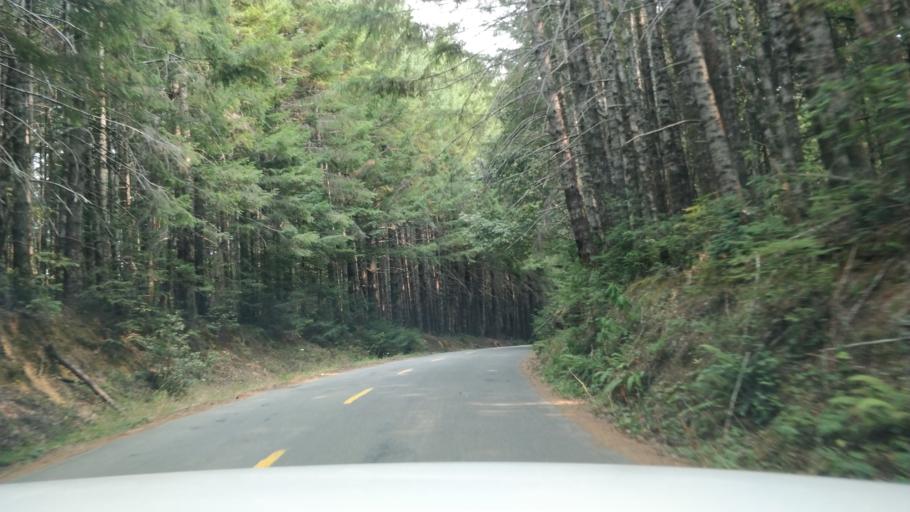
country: US
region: California
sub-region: Humboldt County
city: Westhaven-Moonstone
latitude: 41.2496
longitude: -123.9849
